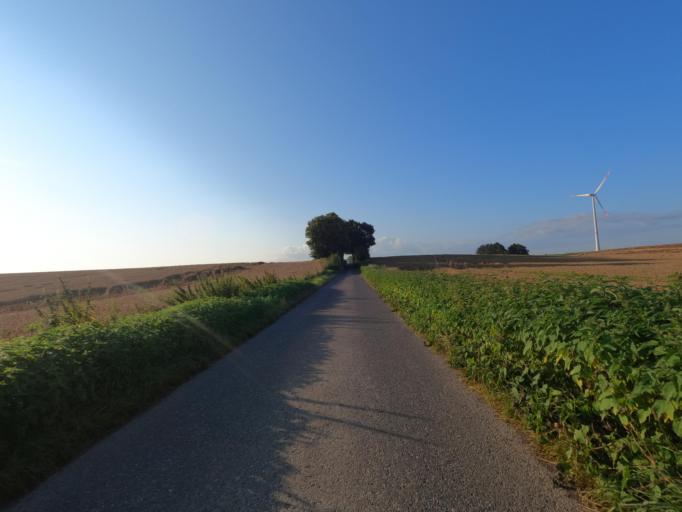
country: DE
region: North Rhine-Westphalia
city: Erkelenz
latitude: 51.0217
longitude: 6.3548
